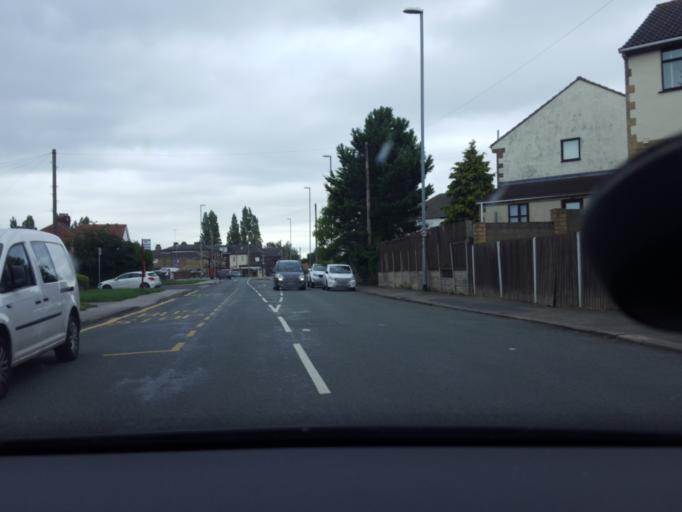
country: GB
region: England
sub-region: City and Borough of Leeds
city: Horsforth
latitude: 53.8187
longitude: -1.6362
